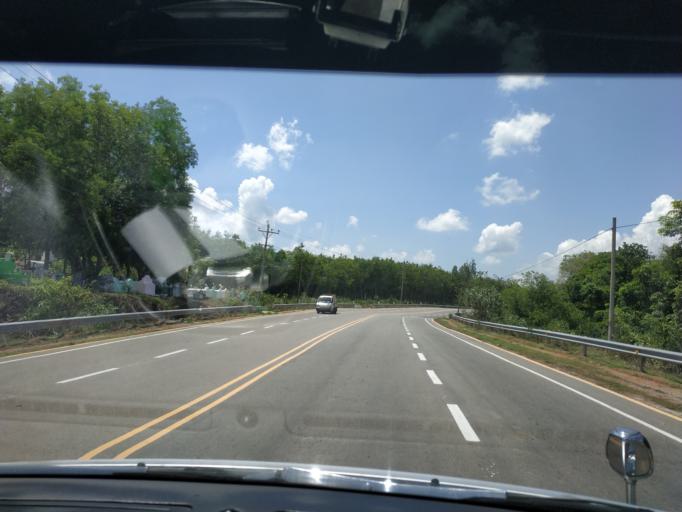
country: MM
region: Mon
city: Kyaikto
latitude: 17.3549
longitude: 97.0397
